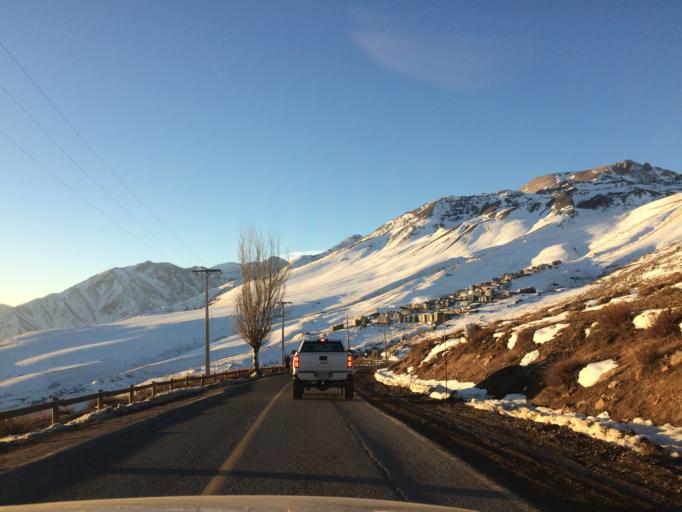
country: CL
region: Santiago Metropolitan
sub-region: Provincia de Santiago
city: Villa Presidente Frei, Nunoa, Santiago, Chile
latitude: -33.3490
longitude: -70.2962
